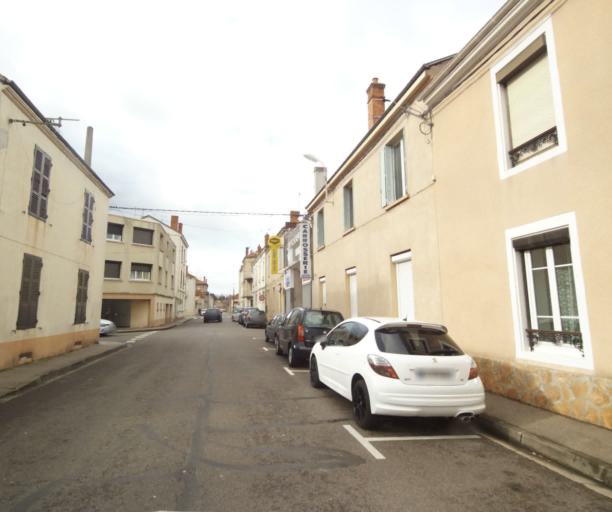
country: FR
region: Rhone-Alpes
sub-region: Departement de la Loire
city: Riorges
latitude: 46.0408
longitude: 4.0589
